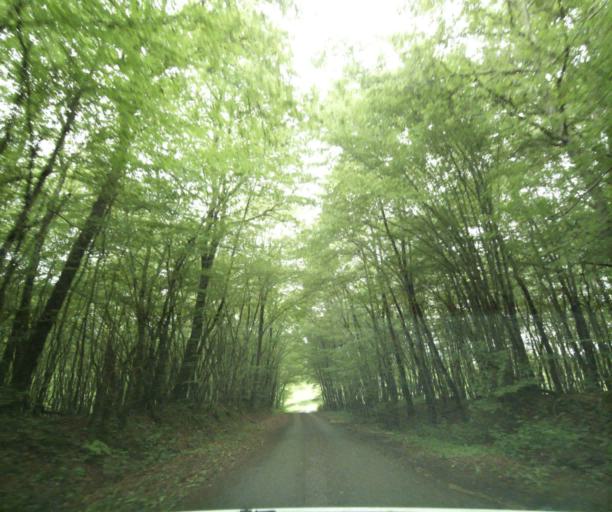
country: FR
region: Bourgogne
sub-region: Departement de Saone-et-Loire
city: Charolles
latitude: 46.4535
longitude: 4.2665
